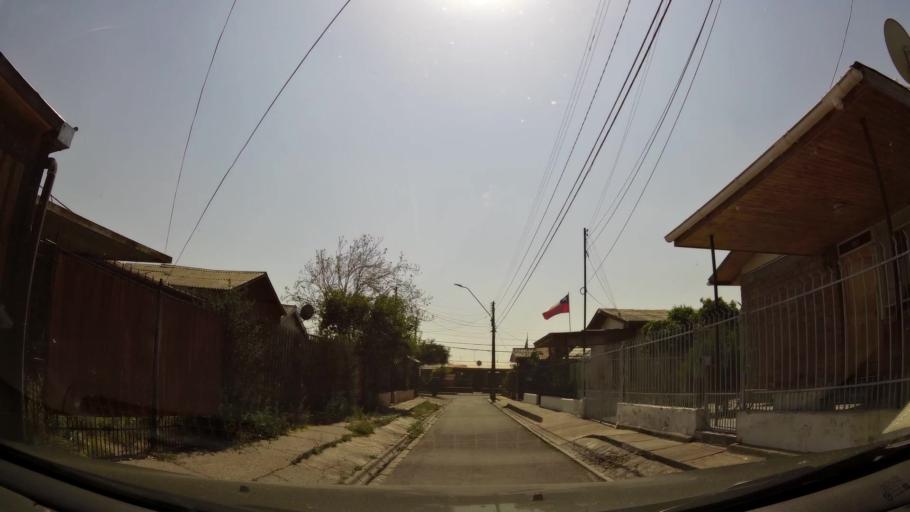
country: CL
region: Santiago Metropolitan
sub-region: Provincia de Maipo
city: San Bernardo
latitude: -33.5836
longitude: -70.7106
